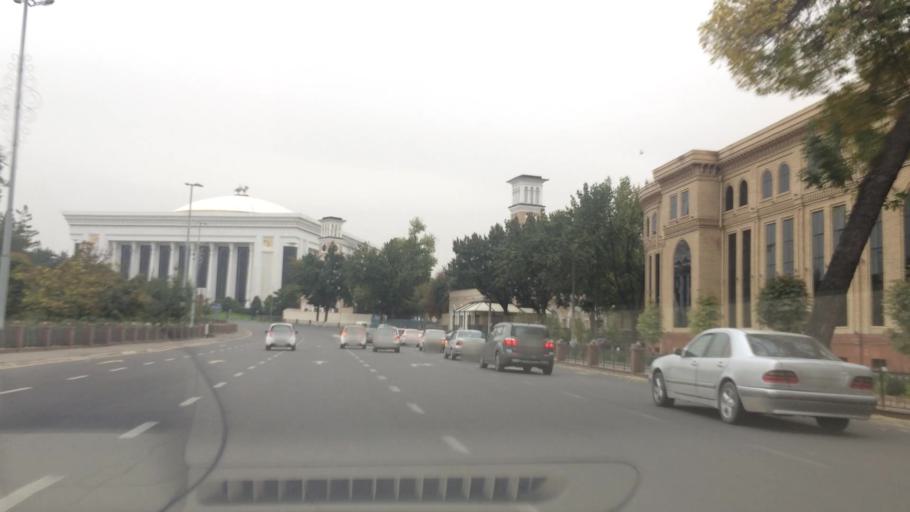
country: UZ
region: Toshkent Shahri
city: Tashkent
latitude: 41.3103
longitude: 69.2782
